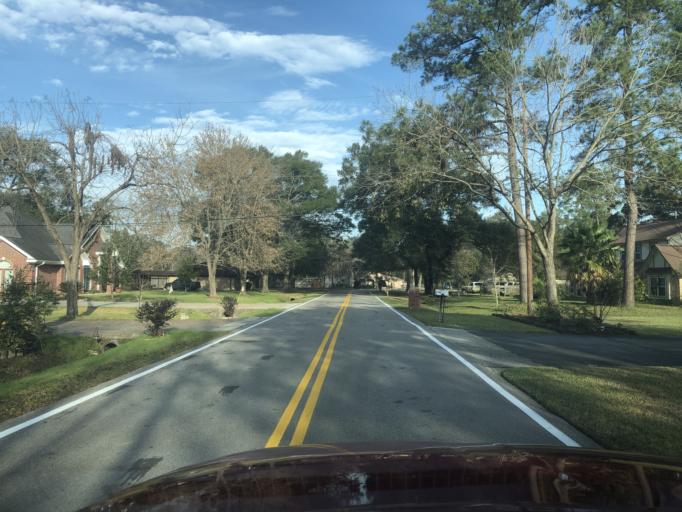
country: US
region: Texas
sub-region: Harris County
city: Spring
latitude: 30.0144
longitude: -95.4732
